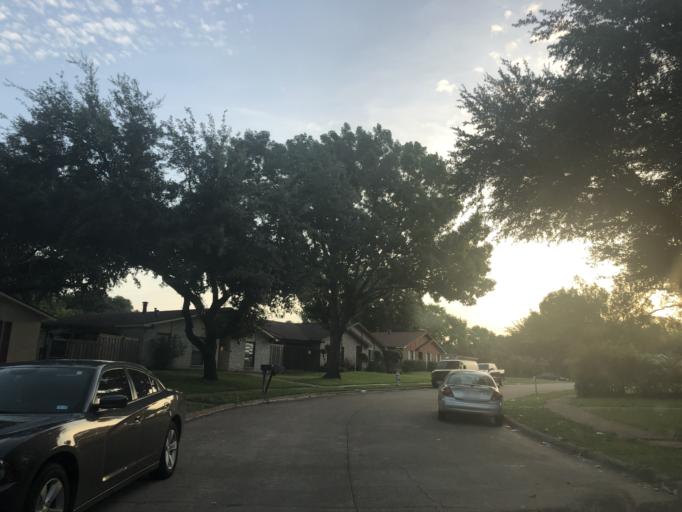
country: US
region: Texas
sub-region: Dallas County
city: Sunnyvale
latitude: 32.8382
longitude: -96.5922
